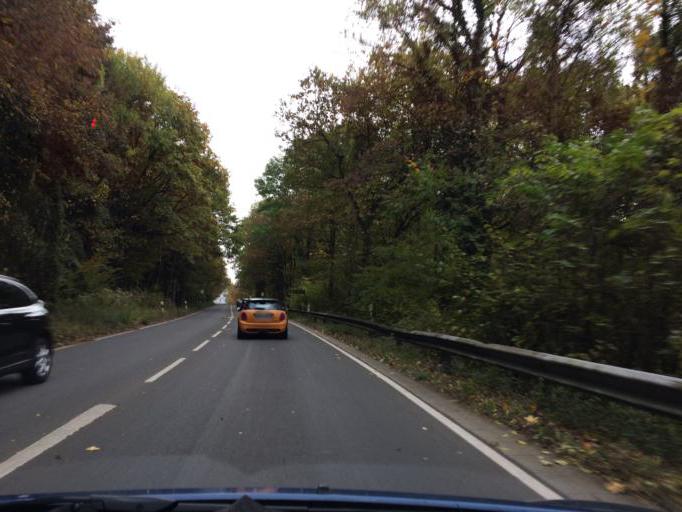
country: DE
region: North Rhine-Westphalia
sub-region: Regierungsbezirk Koln
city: Bad Honnef
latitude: 50.6780
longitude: 7.2453
